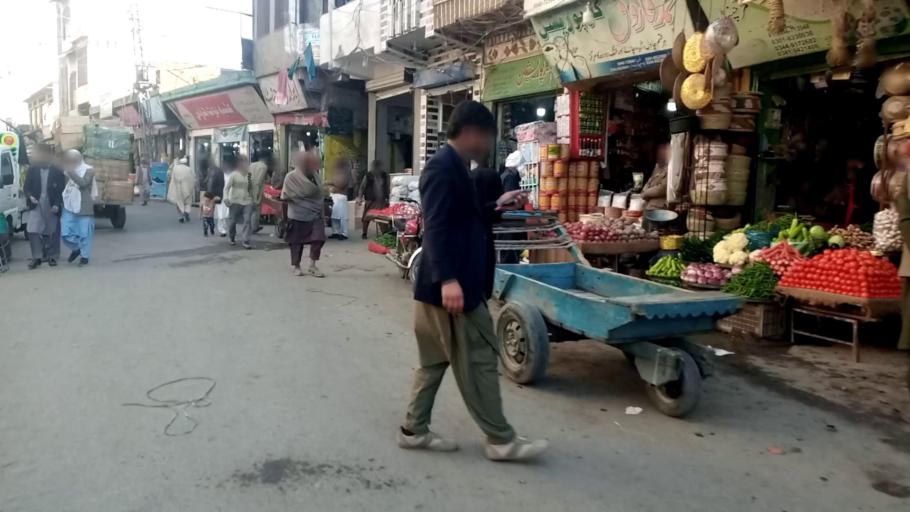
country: PK
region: Khyber Pakhtunkhwa
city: Mingora
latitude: 34.7763
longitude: 72.3581
